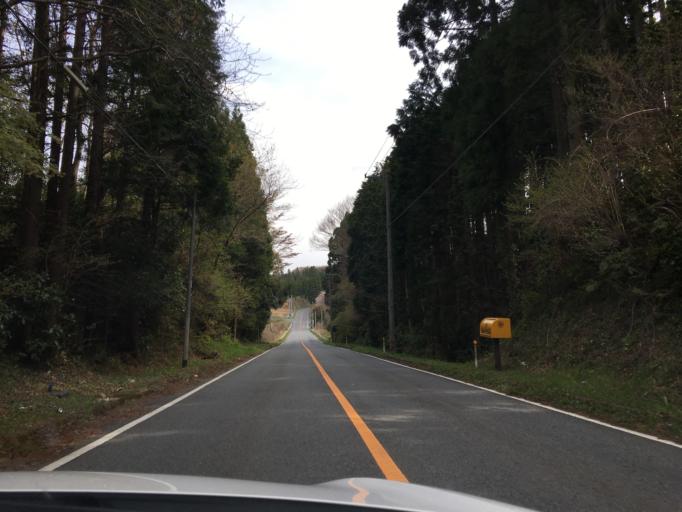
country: JP
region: Fukushima
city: Iwaki
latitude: 37.0597
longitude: 140.8021
